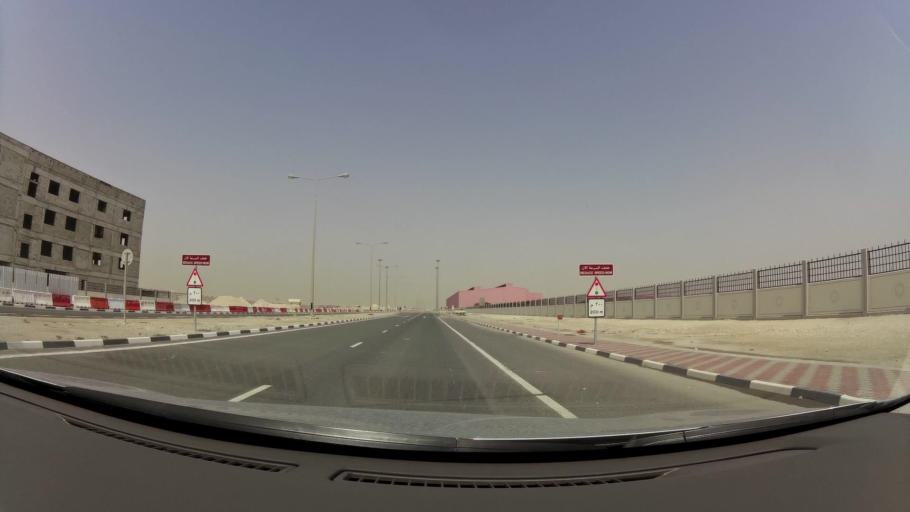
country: QA
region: Al Wakrah
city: Al Wukayr
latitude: 25.1472
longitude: 51.3914
